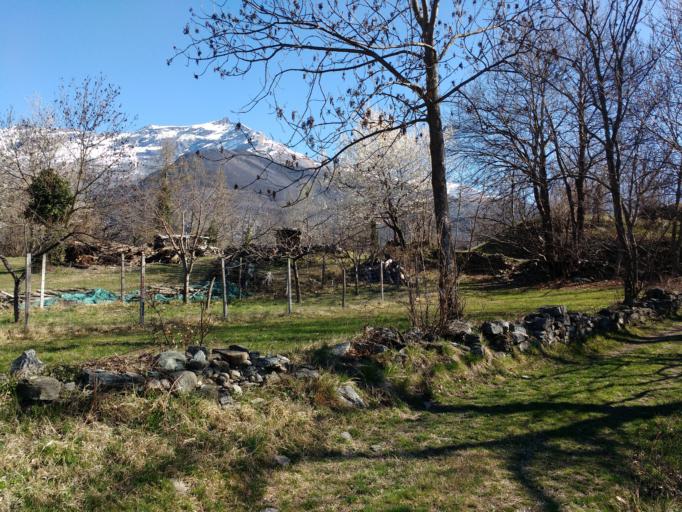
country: IT
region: Piedmont
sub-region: Provincia di Torino
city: Giaglione
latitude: 45.1442
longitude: 7.0103
